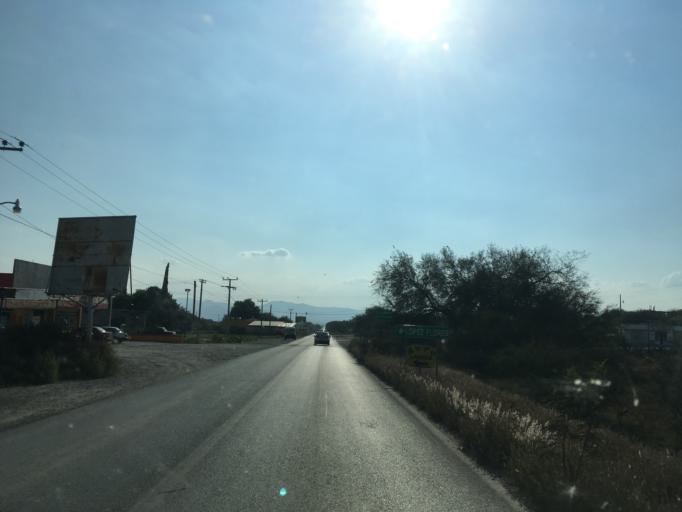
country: MX
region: Hidalgo
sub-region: Ixmiquilpan
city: El Nith
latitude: 20.5554
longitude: -99.1596
